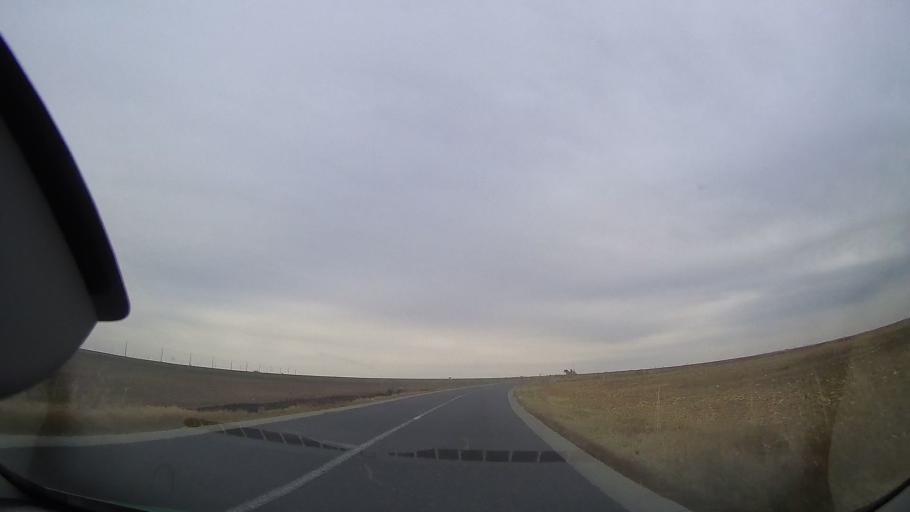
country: RO
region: Ialomita
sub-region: Comuna Milosesti
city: Milosesti
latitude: 44.7579
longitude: 27.2026
